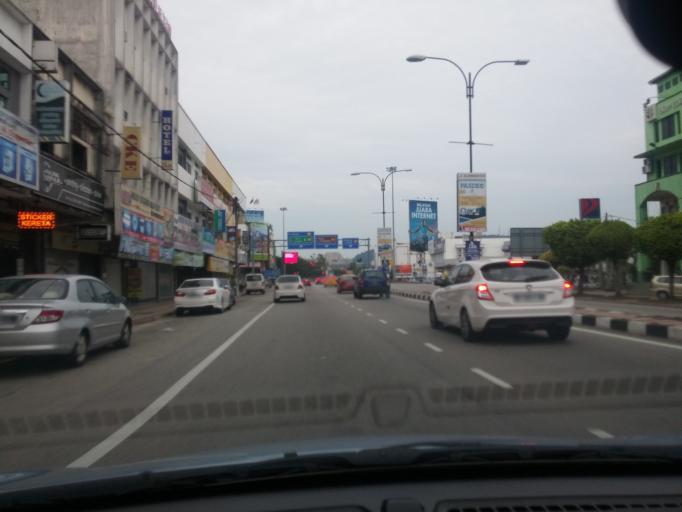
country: MY
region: Pahang
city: Kuantan
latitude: 3.8113
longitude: 103.3320
